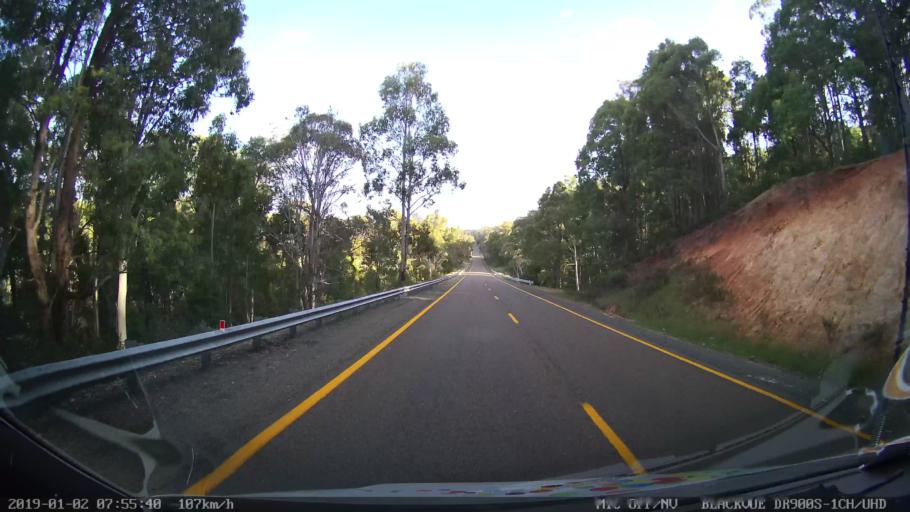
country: AU
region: New South Wales
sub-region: Tumut Shire
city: Tumut
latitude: -35.6812
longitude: 148.4865
